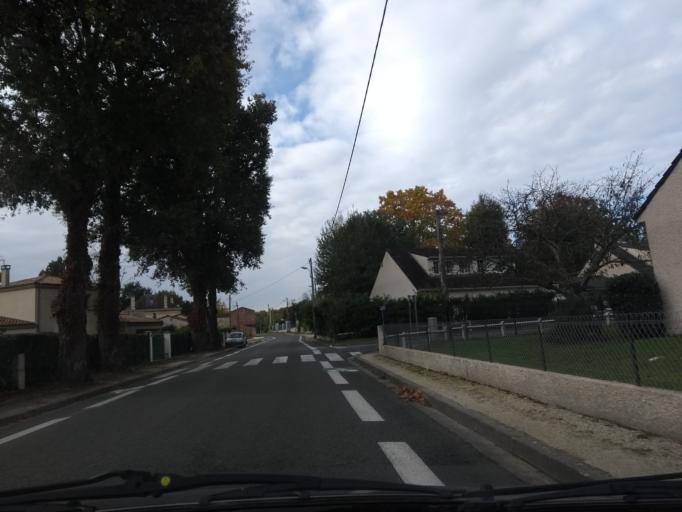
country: FR
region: Aquitaine
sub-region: Departement de la Gironde
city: Gradignan
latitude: 44.7747
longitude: -0.6237
